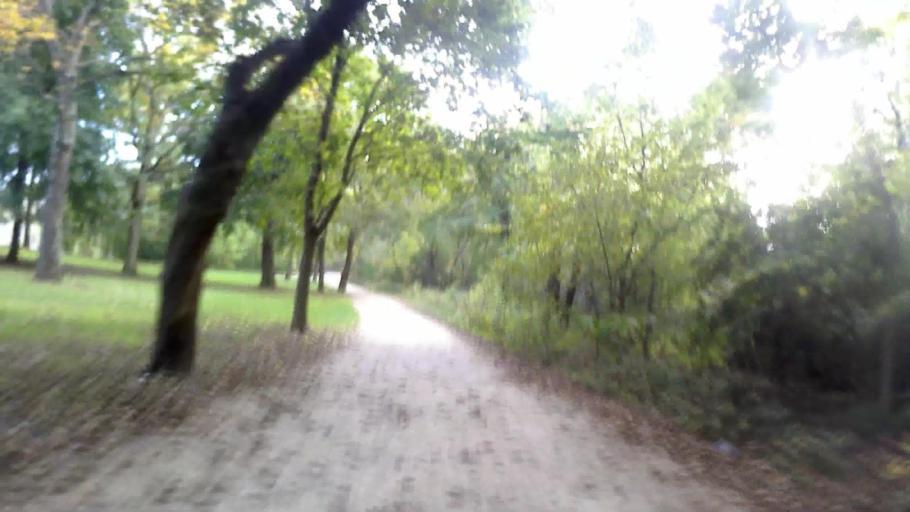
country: US
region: Illinois
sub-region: DuPage County
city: Warrenville
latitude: 41.8287
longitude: -88.1450
